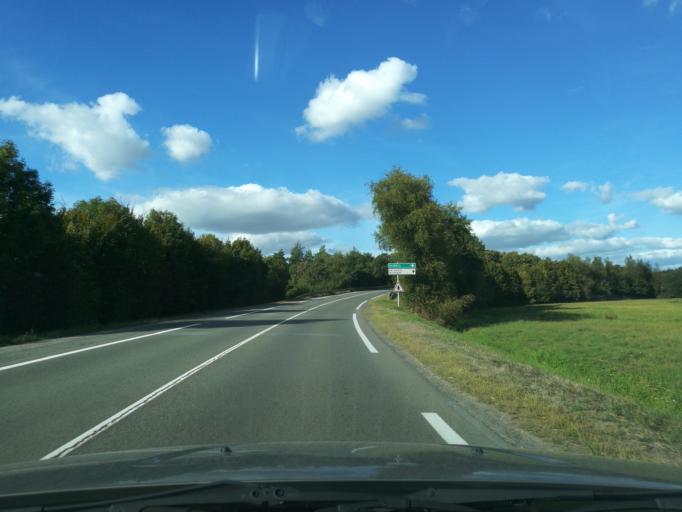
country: FR
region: Brittany
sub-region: Departement d'Ille-et-Vilaine
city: Montauban-de-Bretagne
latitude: 48.2055
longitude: -2.0472
